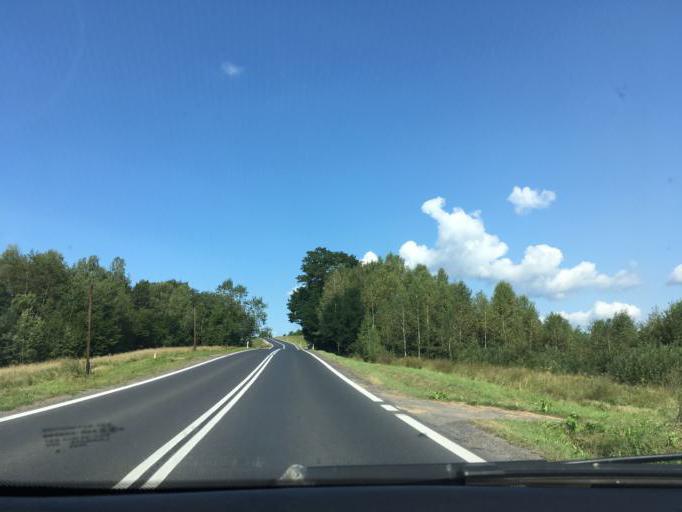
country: PL
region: Subcarpathian Voivodeship
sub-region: Powiat leski
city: Uherce Mineralne
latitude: 49.4665
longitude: 22.3866
